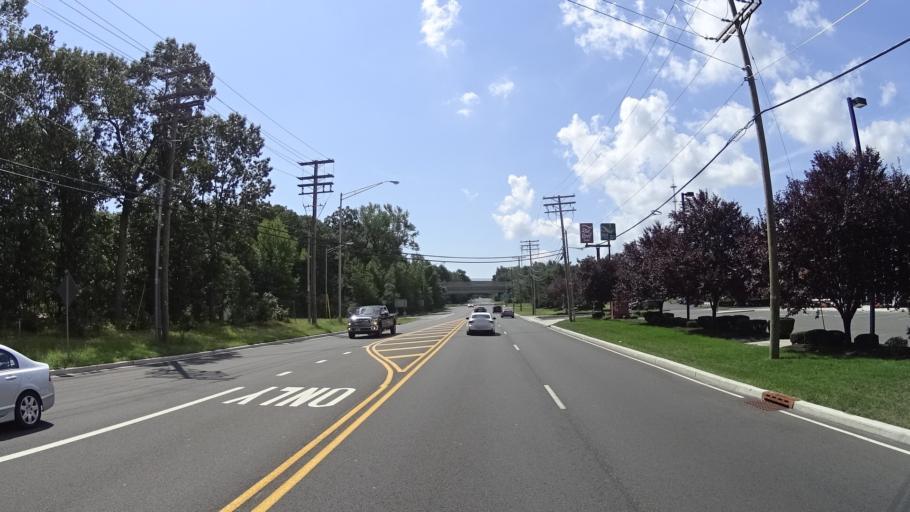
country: US
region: New Jersey
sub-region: Monmouth County
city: Tinton Falls
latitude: 40.2851
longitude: -74.0783
